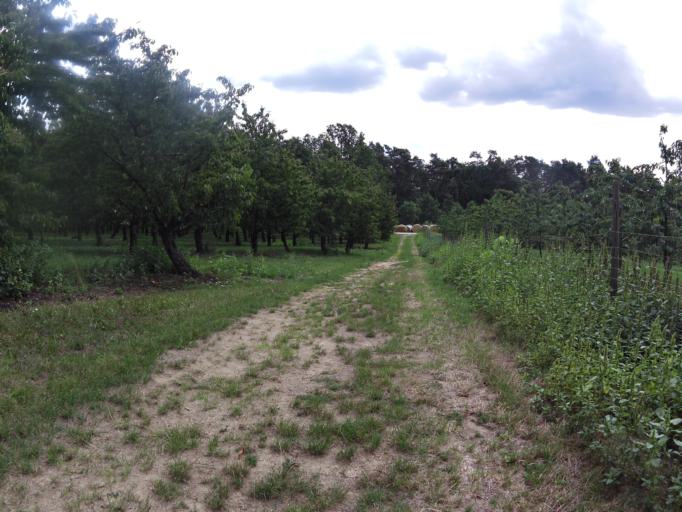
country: DE
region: Bavaria
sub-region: Regierungsbezirk Unterfranken
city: Sommerhausen
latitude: 49.7065
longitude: 10.0358
